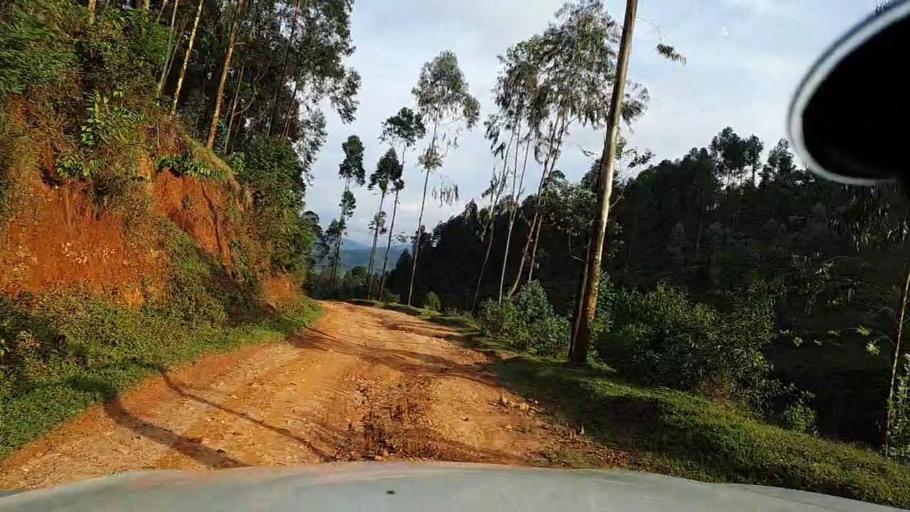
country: RW
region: Southern Province
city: Gitarama
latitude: -2.1868
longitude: 29.5721
